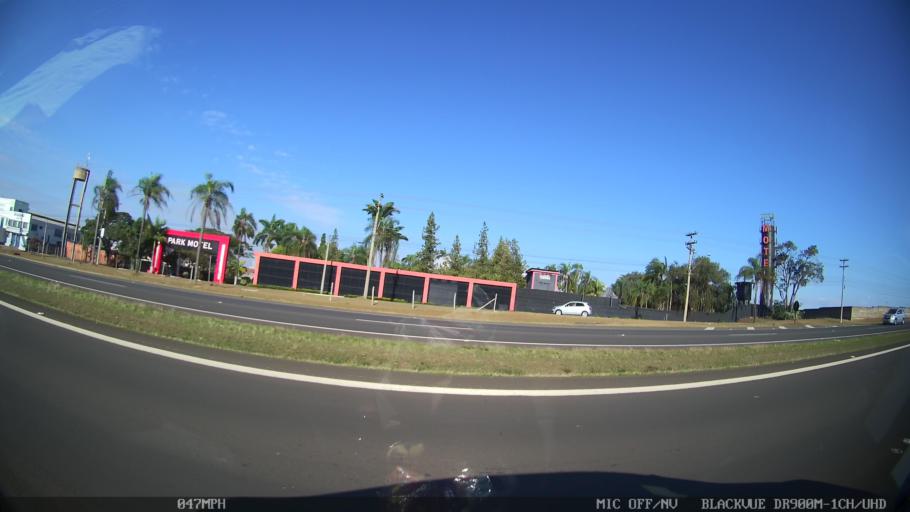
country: BR
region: Sao Paulo
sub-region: Piracicaba
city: Piracicaba
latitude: -22.6863
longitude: -47.6398
